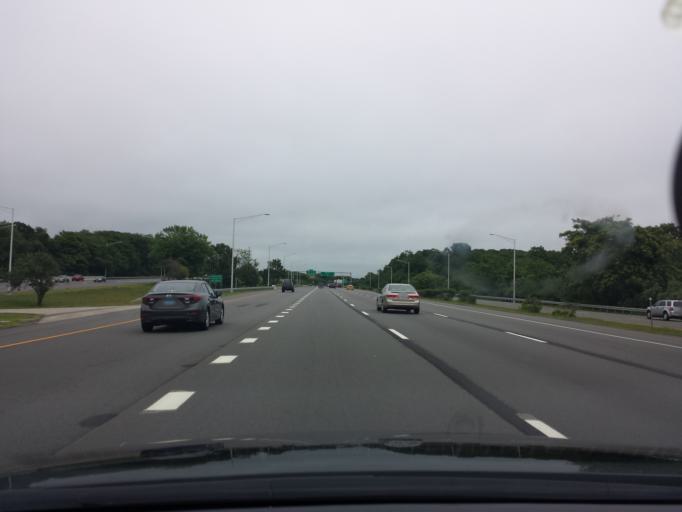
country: US
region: Connecticut
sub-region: New London County
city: Groton
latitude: 41.3643
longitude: -72.0774
